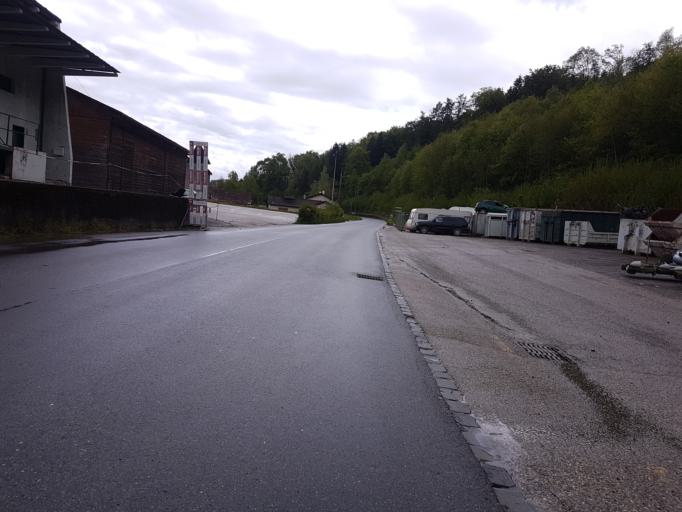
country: CH
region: Vaud
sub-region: Gros-de-Vaud District
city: Penthalaz
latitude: 46.6019
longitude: 6.5246
